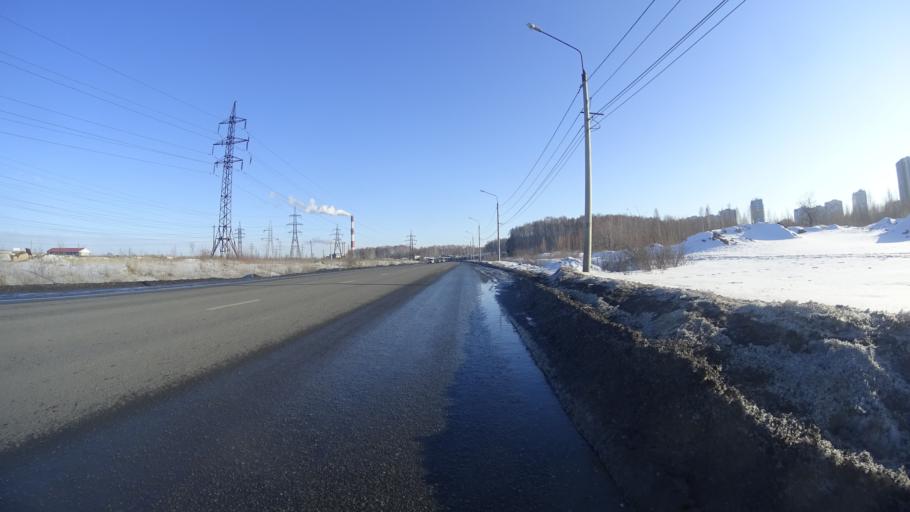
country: RU
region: Chelyabinsk
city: Roshchino
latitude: 55.2135
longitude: 61.3061
